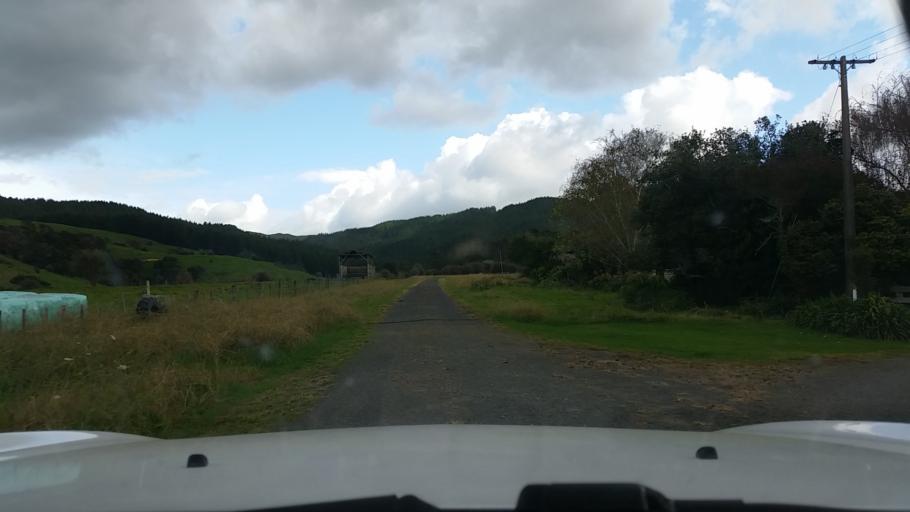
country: NZ
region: Waikato
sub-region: Hauraki District
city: Ngatea
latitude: -37.4371
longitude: 175.4767
